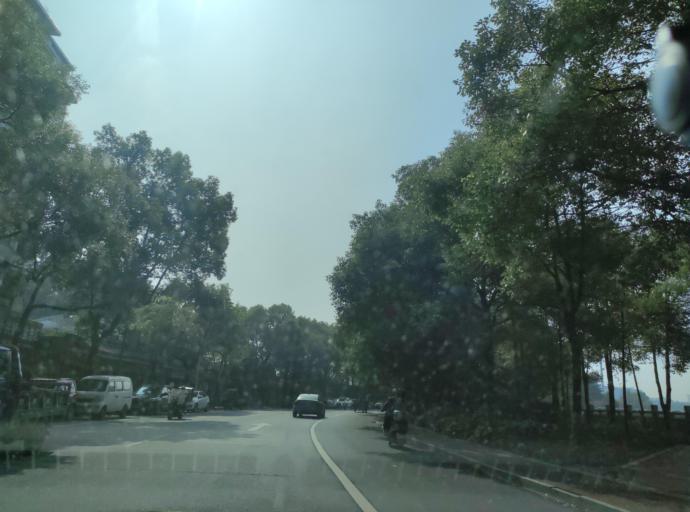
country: CN
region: Jiangxi Sheng
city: Pingxiang
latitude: 27.6418
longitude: 113.8561
